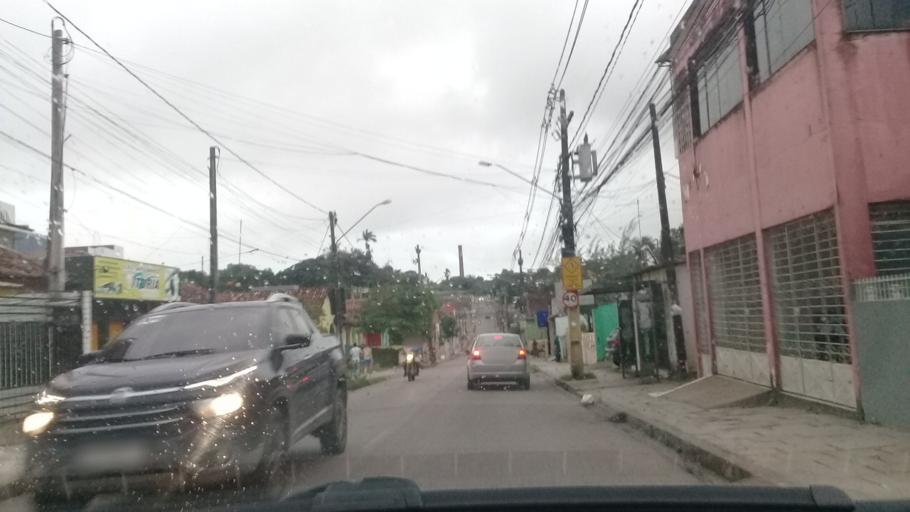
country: BR
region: Pernambuco
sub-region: Moreno
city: Moreno
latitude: -8.1179
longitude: -35.0953
